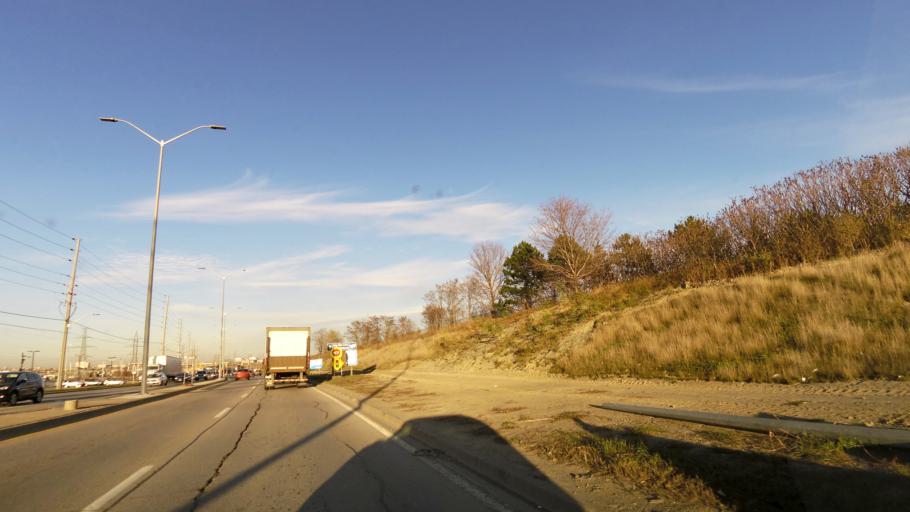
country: CA
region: Ontario
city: Mississauga
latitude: 43.6162
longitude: -79.6280
